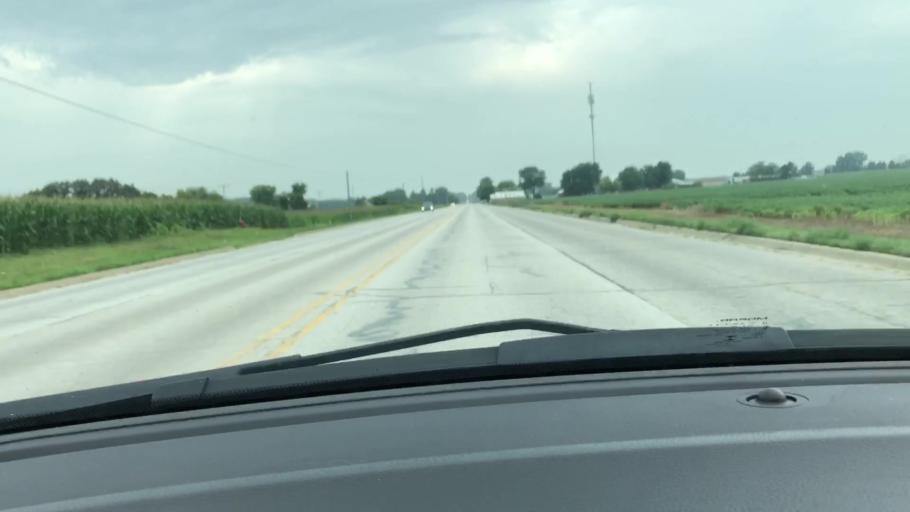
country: US
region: Michigan
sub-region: Saginaw County
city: Shields
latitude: 43.4810
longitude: -84.0647
